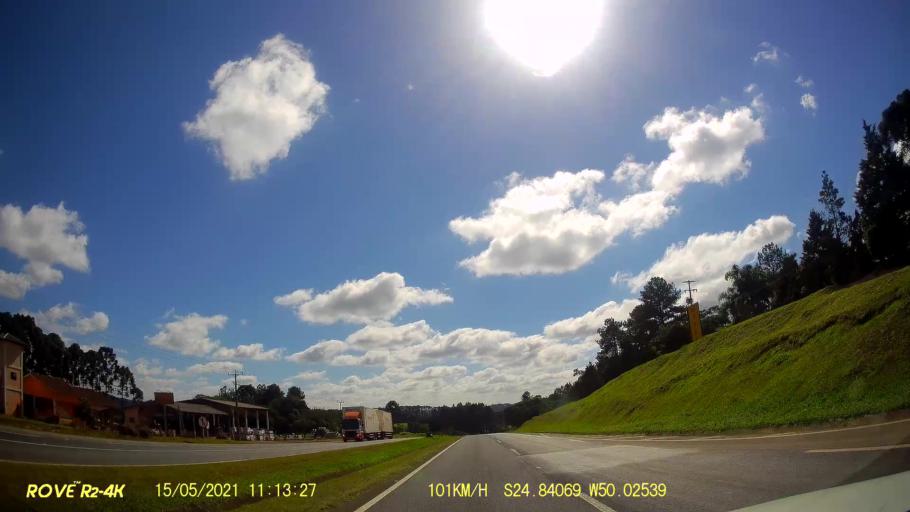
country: BR
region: Parana
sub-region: Castro
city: Castro
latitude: -24.8408
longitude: -50.0253
